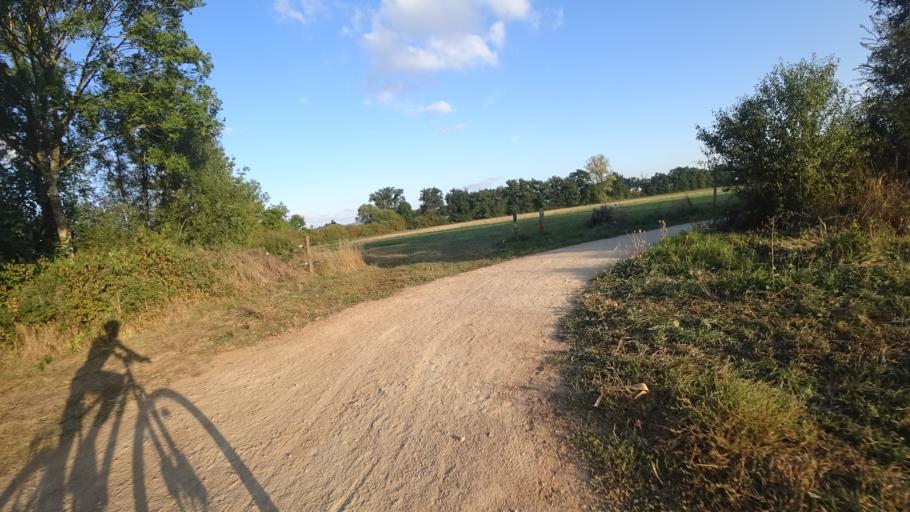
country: FR
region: Midi-Pyrenees
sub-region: Departement de l'Aveyron
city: Rodez
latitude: 44.3789
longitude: 2.5835
